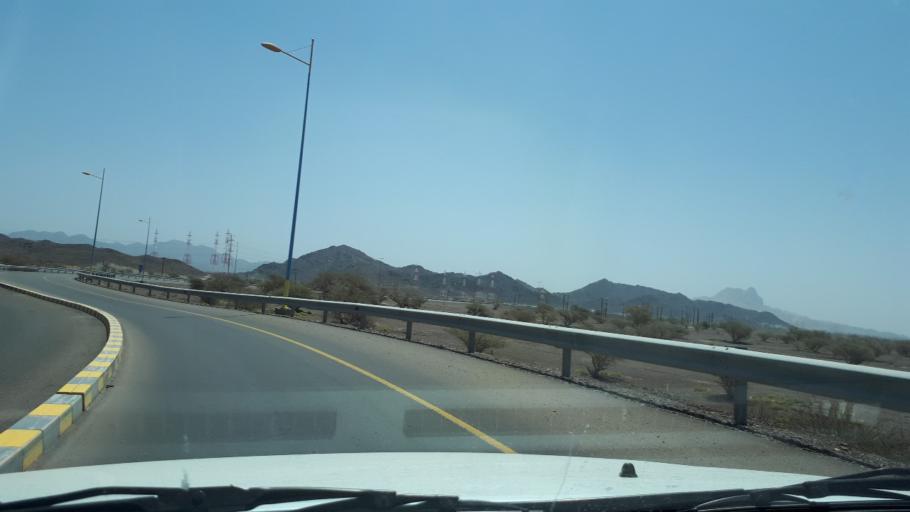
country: OM
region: Muhafazat ad Dakhiliyah
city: Bahla'
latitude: 22.9248
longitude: 57.2565
